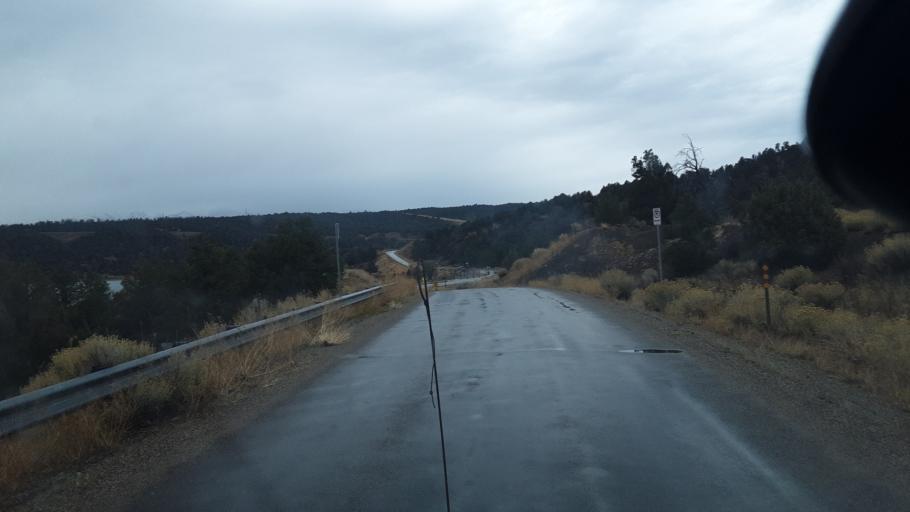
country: US
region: Colorado
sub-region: La Plata County
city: Durango
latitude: 37.2312
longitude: -107.9056
